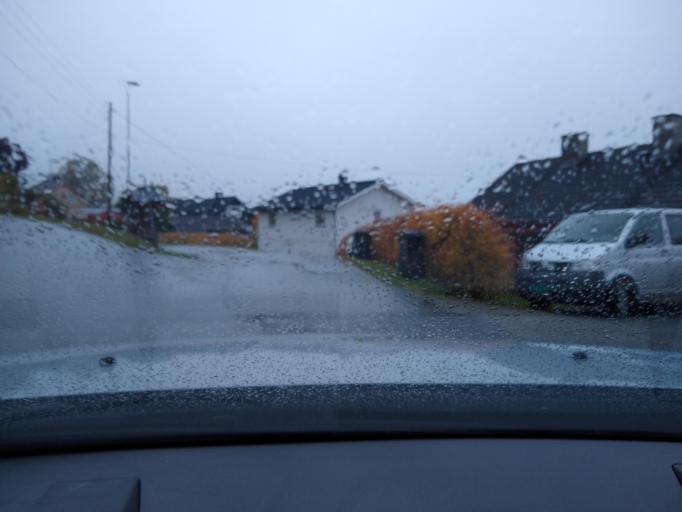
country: NO
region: Oppland
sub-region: Ringebu
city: Ringebu
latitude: 61.5324
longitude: 10.1472
